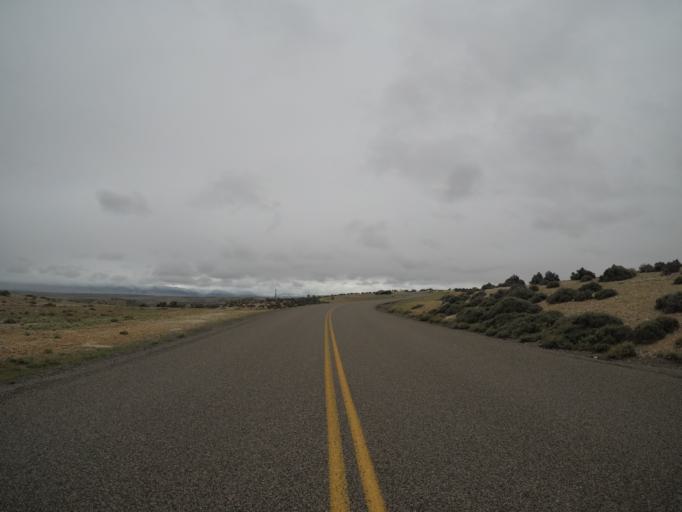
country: US
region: Wyoming
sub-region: Big Horn County
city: Lovell
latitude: 45.0224
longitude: -108.2526
